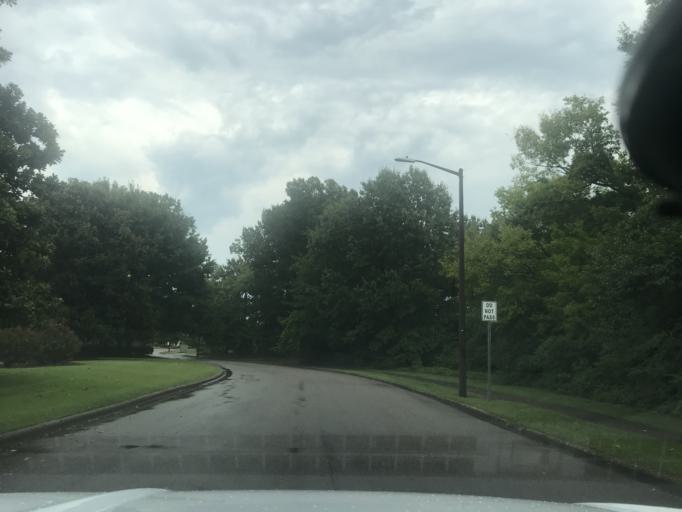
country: US
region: Alabama
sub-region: Montgomery County
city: Pike Road
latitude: 32.3679
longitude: -86.1703
